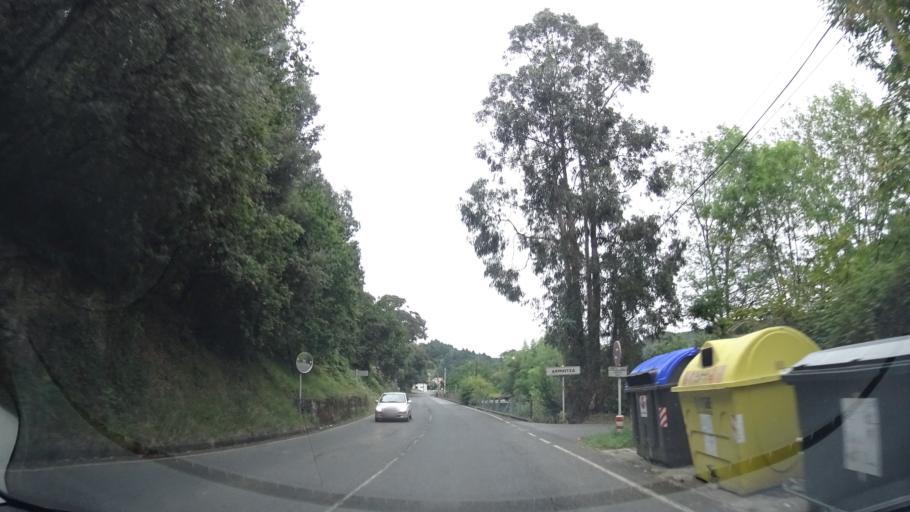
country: ES
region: Basque Country
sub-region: Bizkaia
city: Elexalde
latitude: 43.4292
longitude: -2.8981
